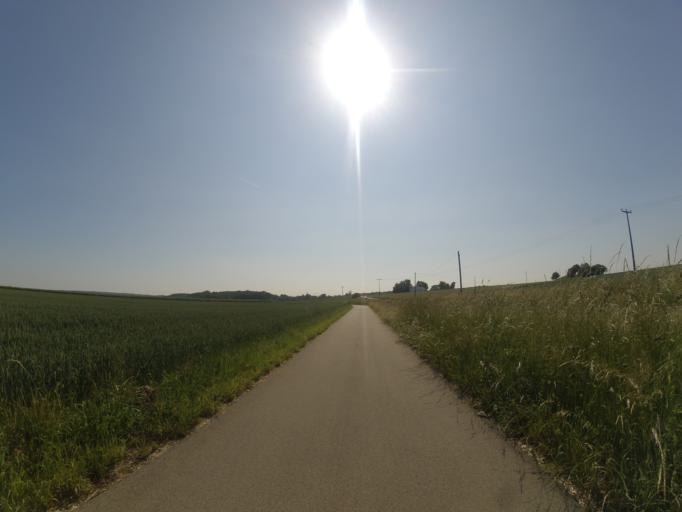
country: DE
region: Baden-Wuerttemberg
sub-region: Tuebingen Region
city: Beimerstetten
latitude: 48.4829
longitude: 9.9935
